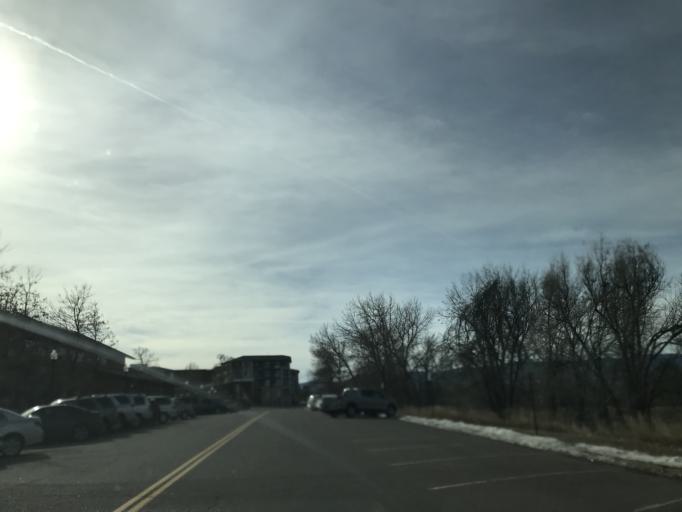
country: US
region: Colorado
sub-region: Arapahoe County
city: Littleton
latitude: 39.6149
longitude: -105.0125
